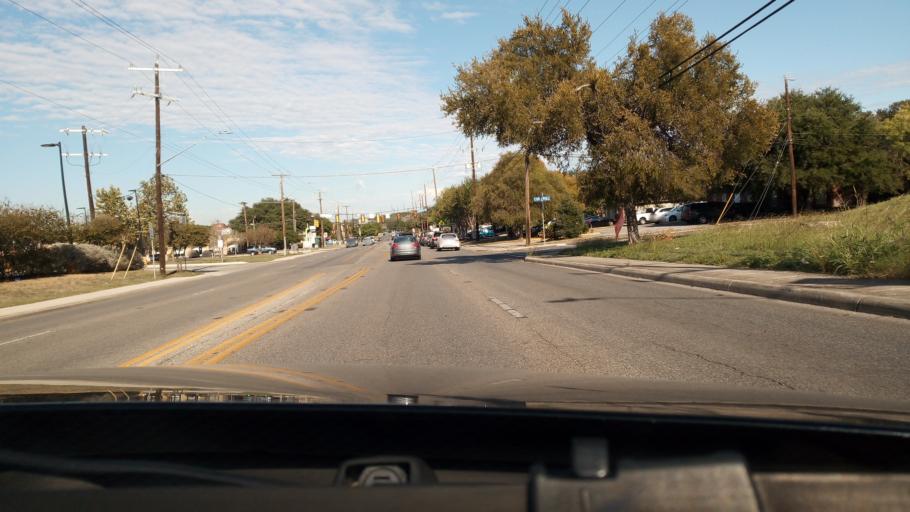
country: US
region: Texas
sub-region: Bexar County
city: Alamo Heights
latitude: 29.5266
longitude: -98.4383
